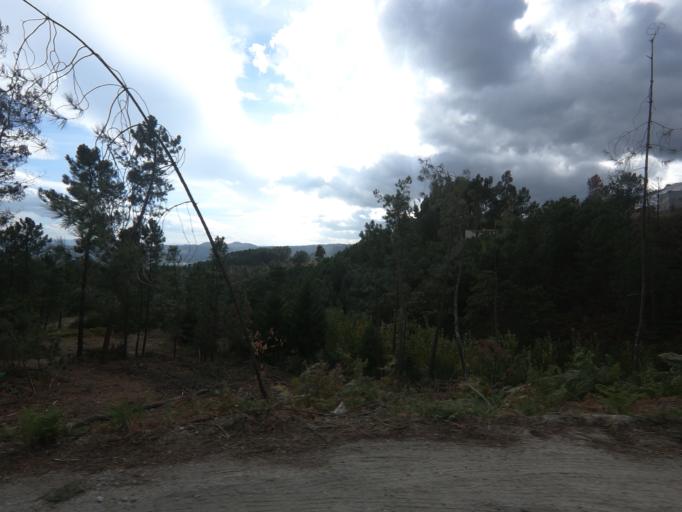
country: PT
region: Vila Real
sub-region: Vila Real
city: Vila Real
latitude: 41.3218
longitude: -7.7768
